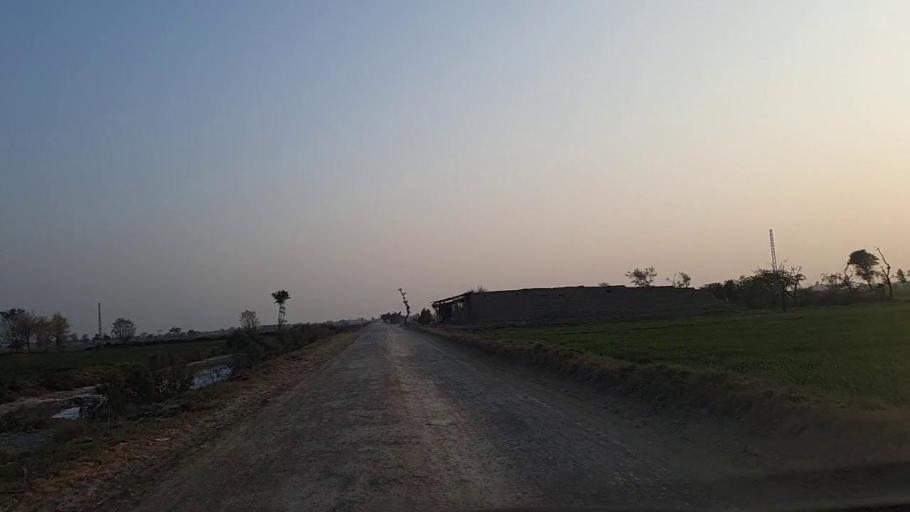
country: PK
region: Sindh
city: Daur
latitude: 26.4296
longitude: 68.3680
